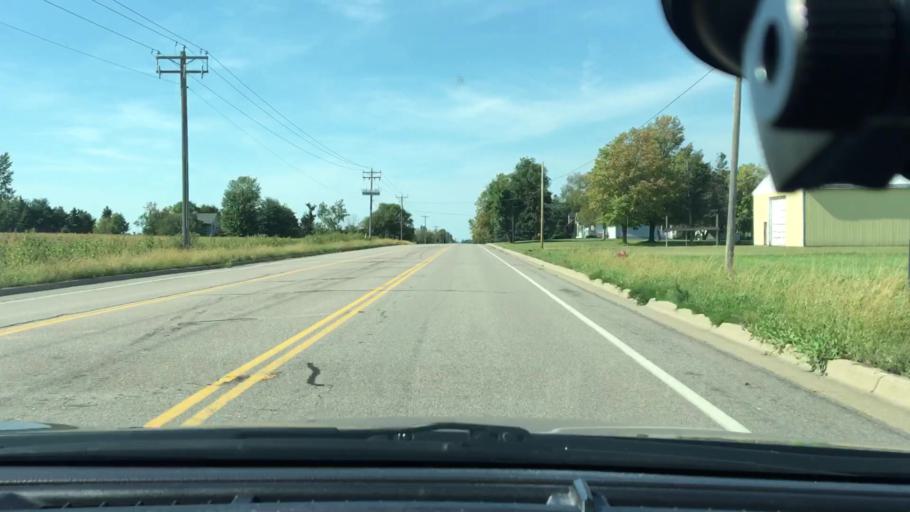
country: US
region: Minnesota
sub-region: Wright County
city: Saint Michael
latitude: 45.1957
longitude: -93.6663
